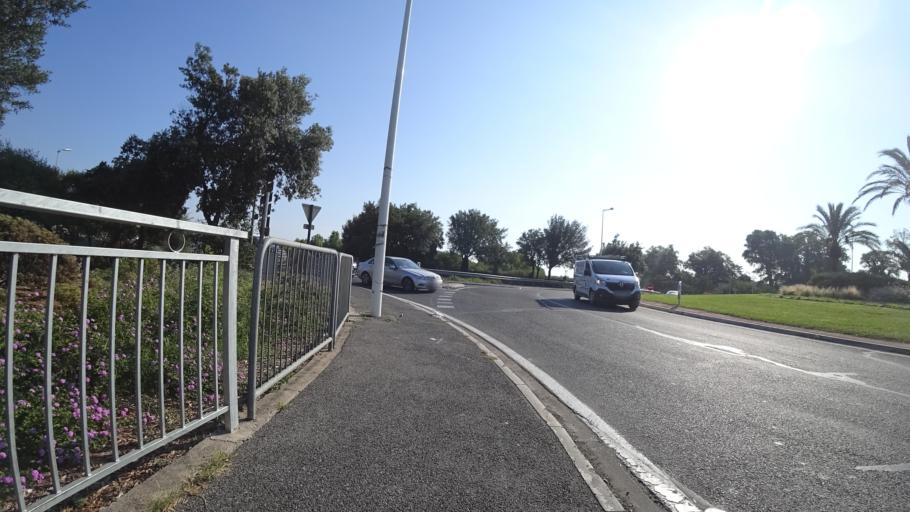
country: FR
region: Languedoc-Roussillon
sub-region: Departement des Pyrenees-Orientales
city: Perpignan
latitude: 42.7076
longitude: 2.9090
